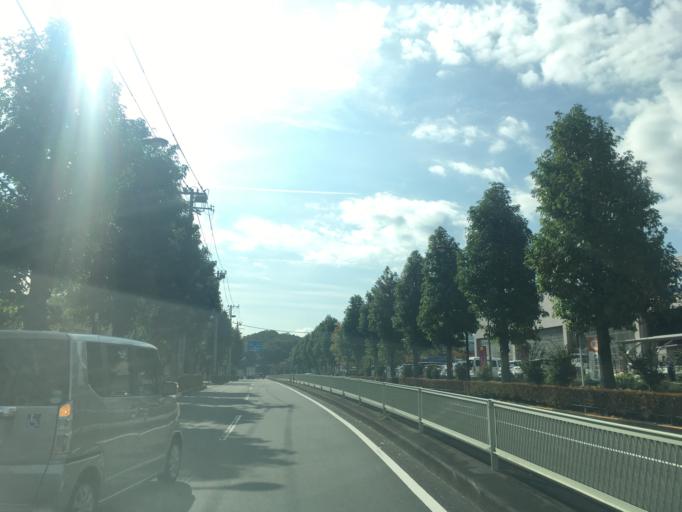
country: JP
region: Tokyo
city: Hino
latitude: 35.6153
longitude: 139.4119
